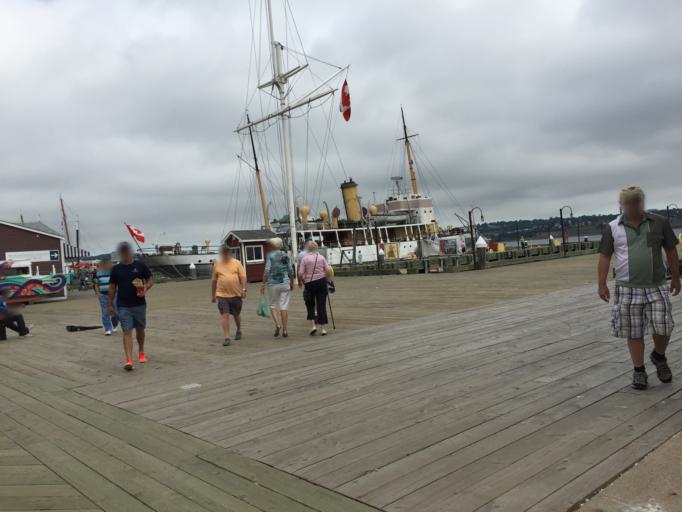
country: CA
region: Nova Scotia
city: Halifax
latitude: 44.6474
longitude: -63.5703
